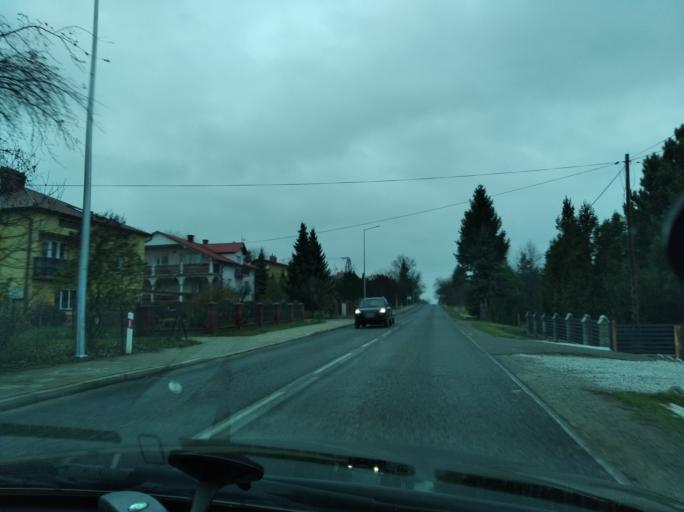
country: PL
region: Subcarpathian Voivodeship
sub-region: Powiat przeworski
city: Sietesz
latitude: 50.0009
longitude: 22.3508
